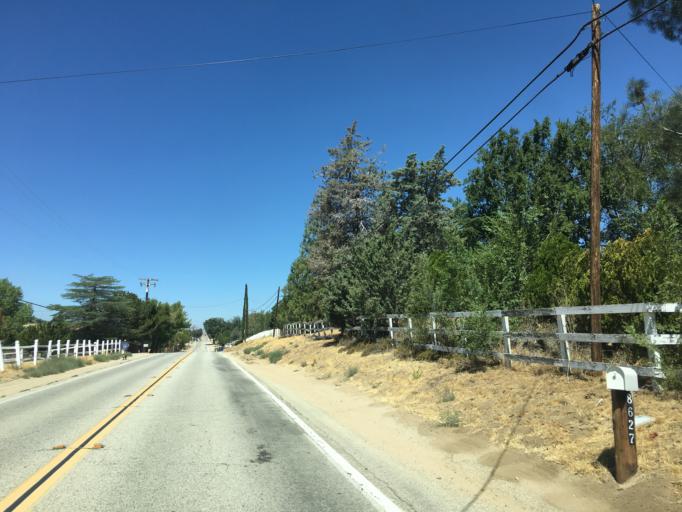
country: US
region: California
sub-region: Los Angeles County
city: Leona Valley
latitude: 34.6161
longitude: -118.2830
